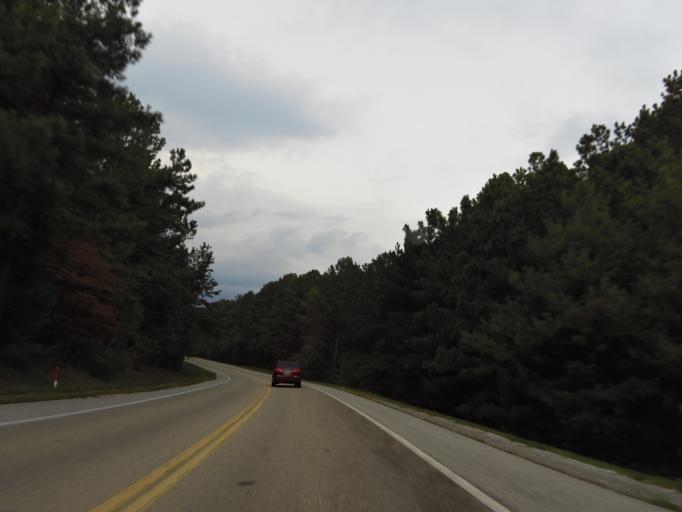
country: US
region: Tennessee
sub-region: Loudon County
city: Loudon
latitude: 35.6985
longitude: -84.2555
